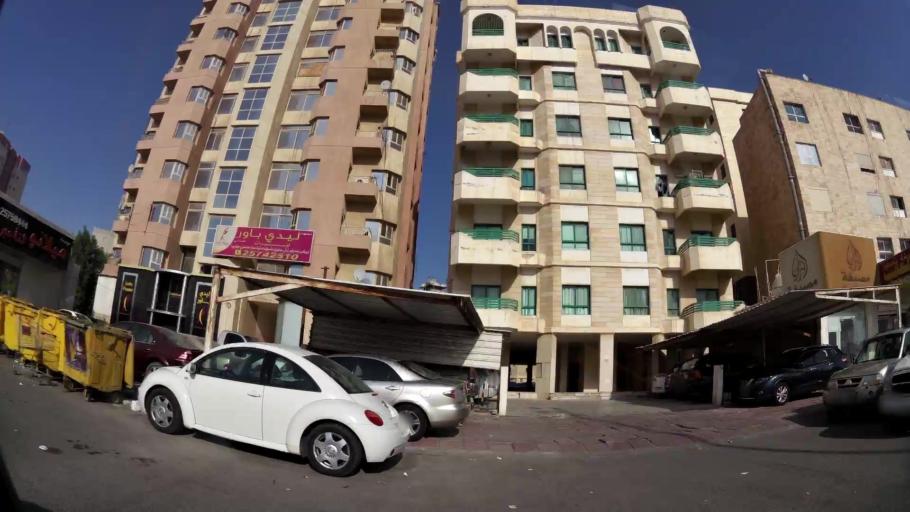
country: KW
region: Muhafazat Hawalli
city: As Salimiyah
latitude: 29.3265
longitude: 48.0849
